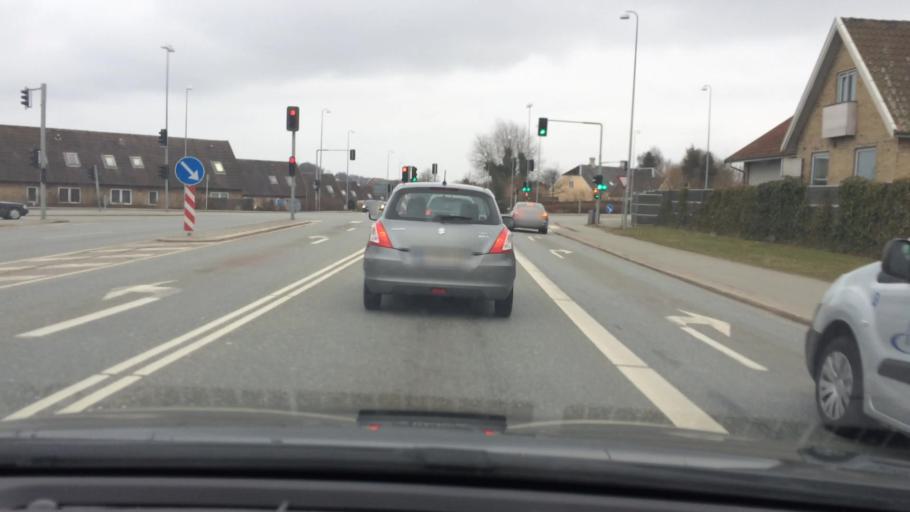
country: DK
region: Central Jutland
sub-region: Horsens Kommune
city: Horsens
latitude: 55.8747
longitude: 9.8228
